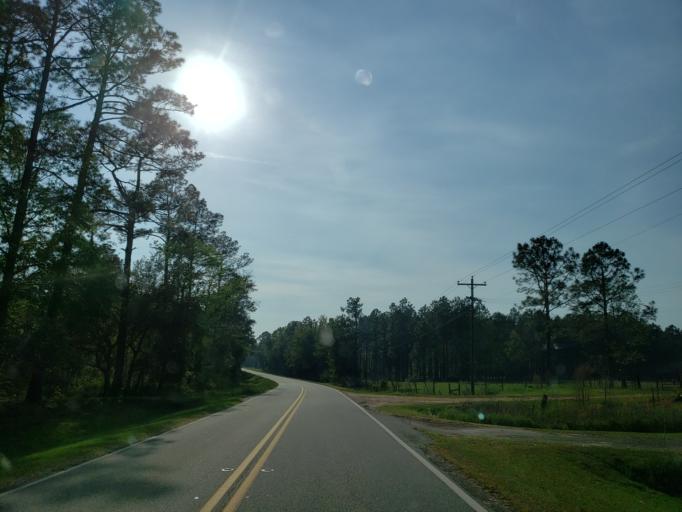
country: US
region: Georgia
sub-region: Tift County
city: Tifton
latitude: 31.5586
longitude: -83.5015
